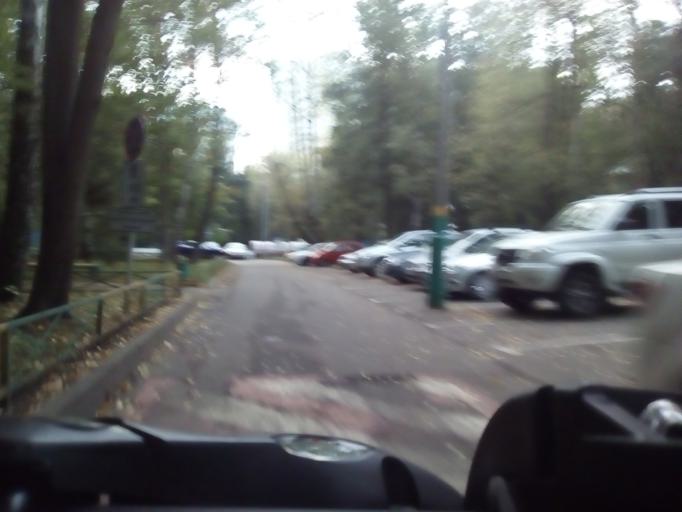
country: RU
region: Moscow
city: Sviblovo
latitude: 55.8496
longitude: 37.6411
